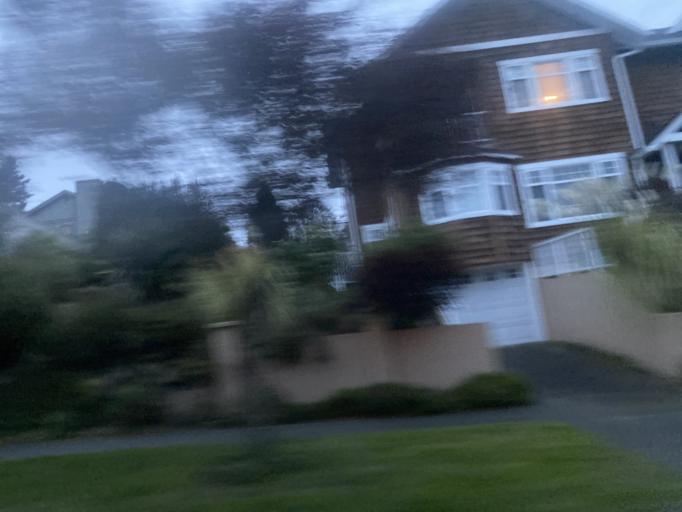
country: US
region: Washington
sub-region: King County
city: Seattle
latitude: 47.6385
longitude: -122.3942
